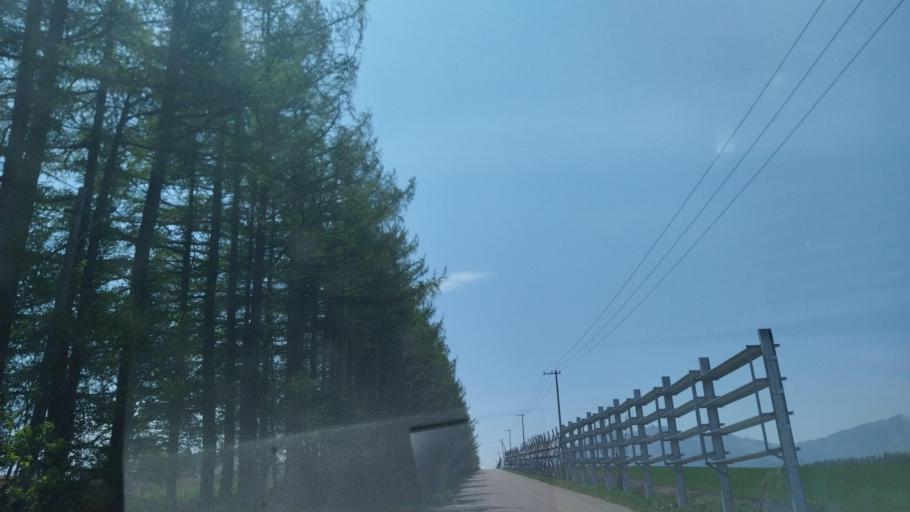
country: JP
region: Hokkaido
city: Obihiro
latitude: 42.9071
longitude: 142.9897
